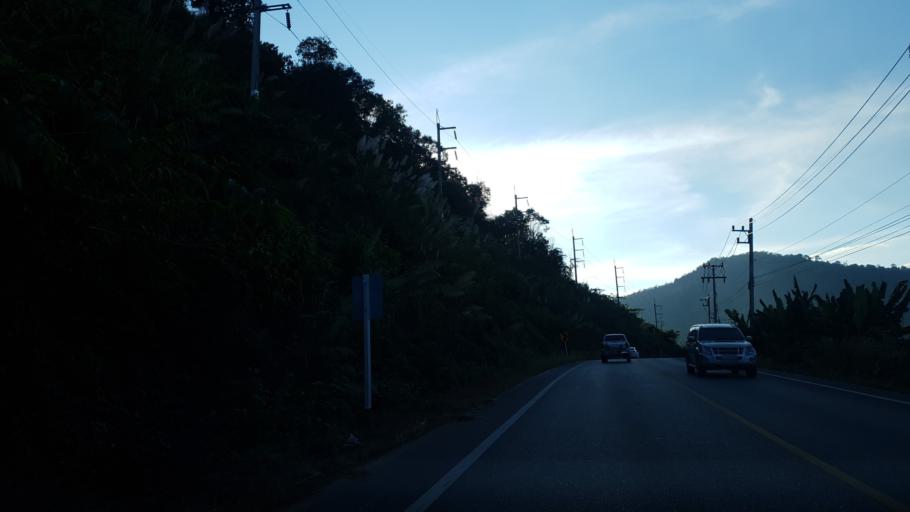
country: TH
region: Loei
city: Dan Sai
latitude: 17.2277
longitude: 101.0413
